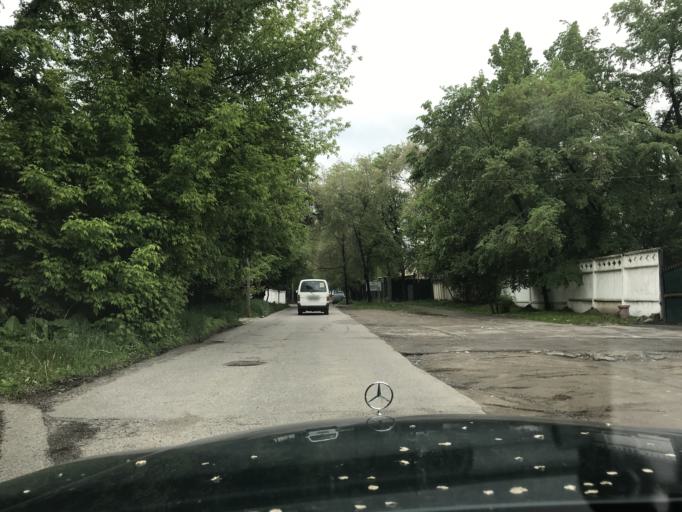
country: KZ
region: Almaty Qalasy
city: Almaty
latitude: 43.2075
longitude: 76.8697
